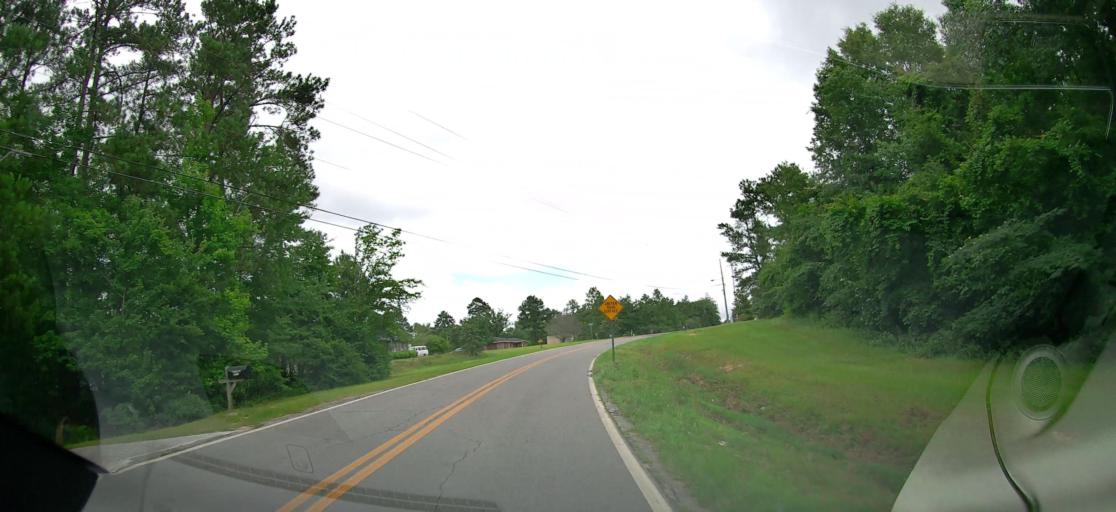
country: US
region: Georgia
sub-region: Bibb County
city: West Point
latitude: 32.7521
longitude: -83.7644
